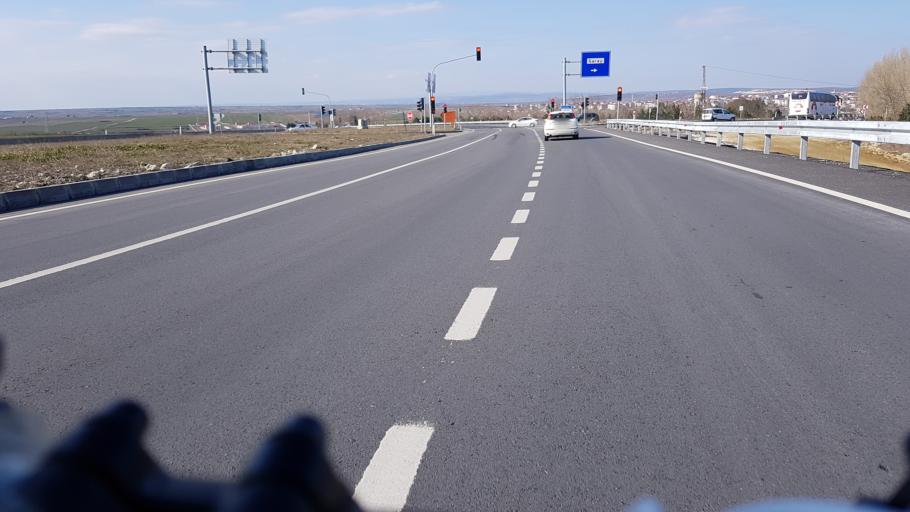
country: TR
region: Tekirdag
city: Saray
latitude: 41.4174
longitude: 27.9221
